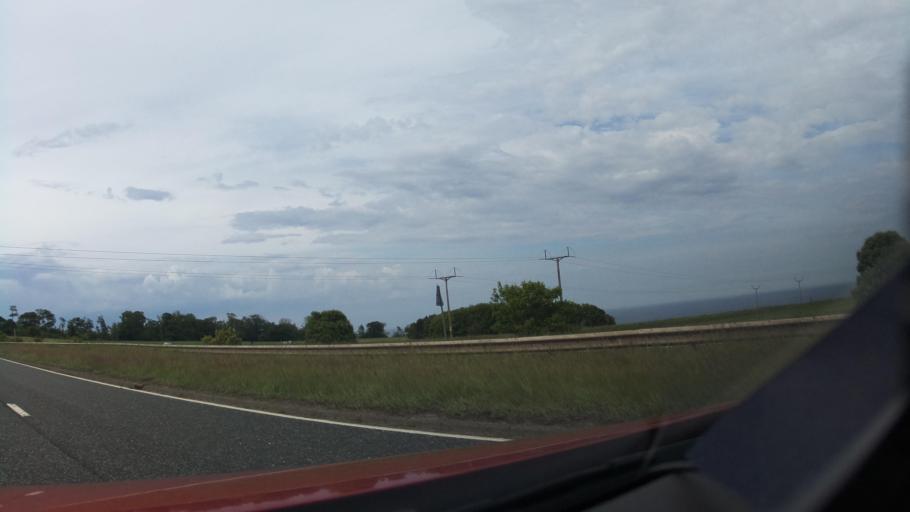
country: GB
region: England
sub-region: Northumberland
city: Berwick-Upon-Tweed
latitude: 55.7971
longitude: -2.0327
